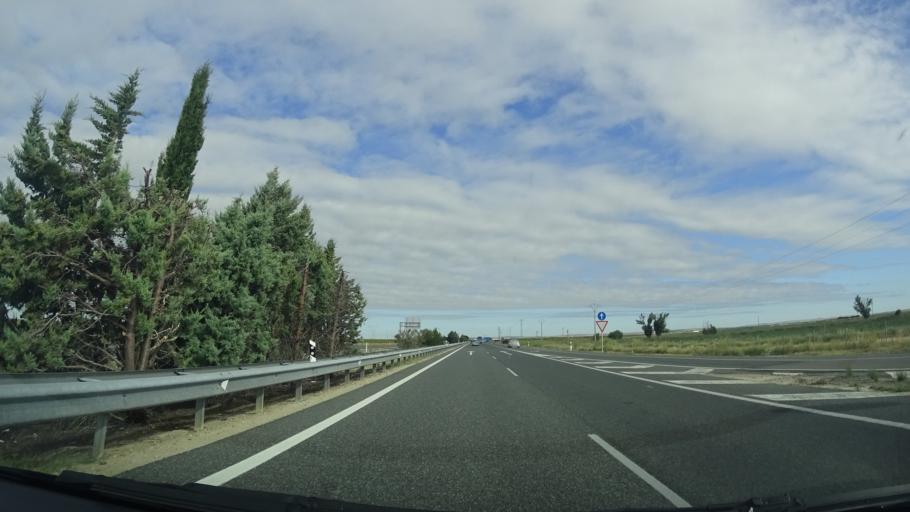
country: ES
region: Castille and Leon
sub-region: Provincia de Valladolid
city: San Vicente del Palacio
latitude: 41.2229
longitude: -4.8449
